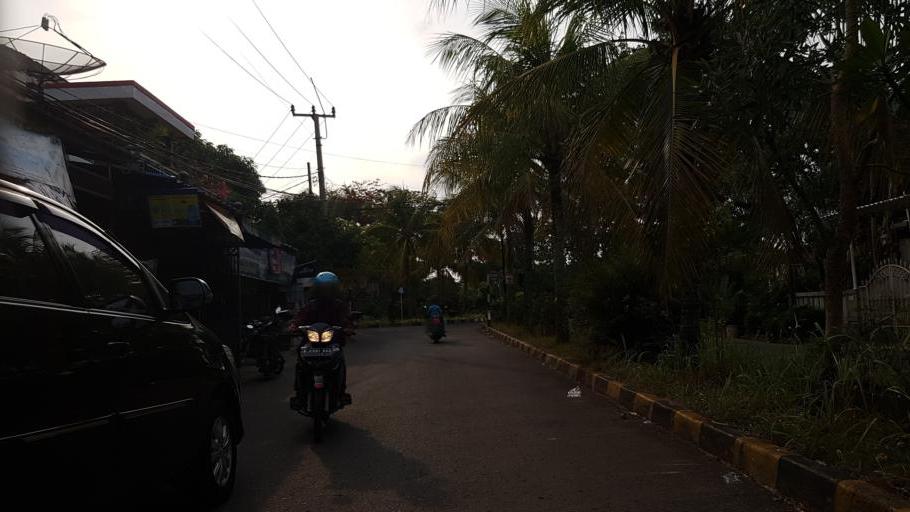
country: ID
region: West Java
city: Sawangan
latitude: -6.3722
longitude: 106.7926
